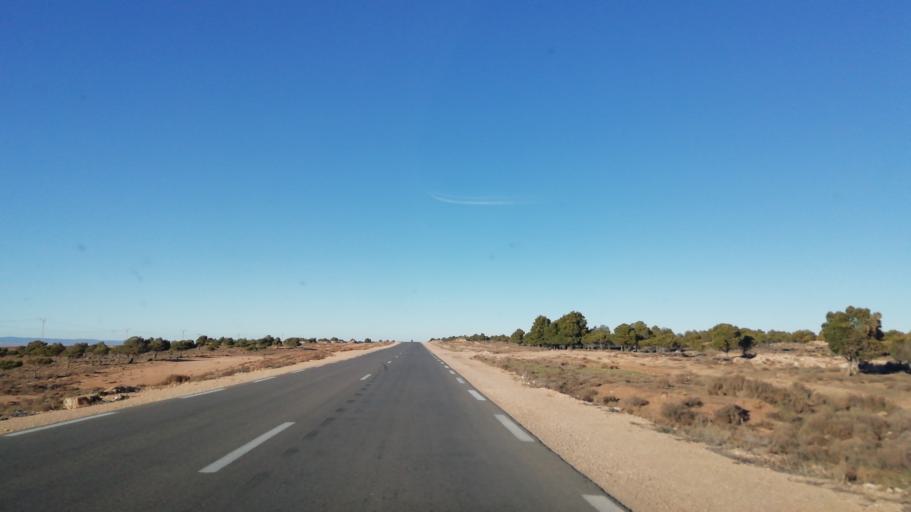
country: DZ
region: Tlemcen
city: Sebdou
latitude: 34.2696
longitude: -1.2584
